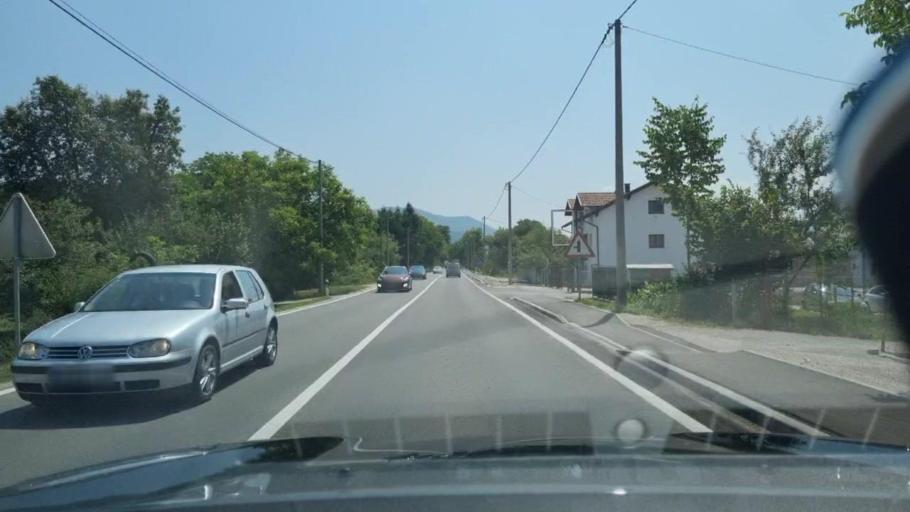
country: BA
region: Federation of Bosnia and Herzegovina
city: Bihac
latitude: 44.7948
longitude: 15.9219
